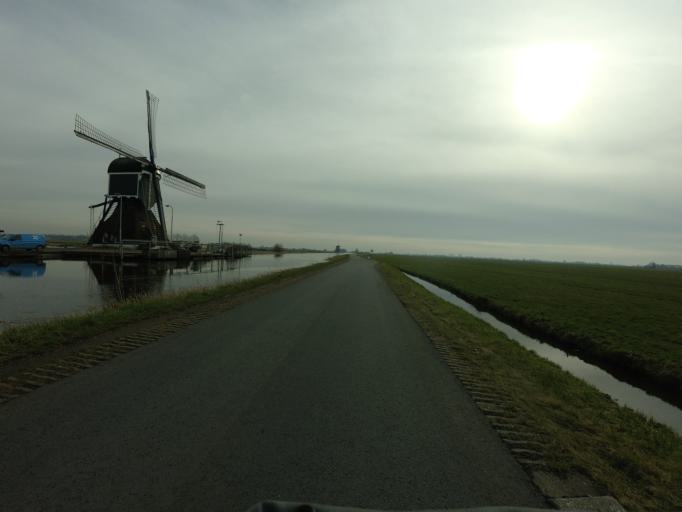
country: NL
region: South Holland
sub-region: Molenwaard
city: Liesveld
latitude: 51.9156
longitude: 4.8255
